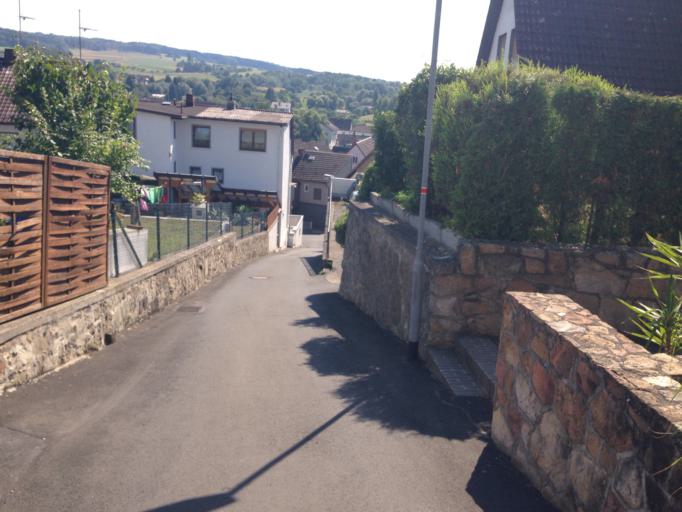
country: DE
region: Hesse
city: Staufenberg
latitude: 50.6689
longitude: 8.7831
